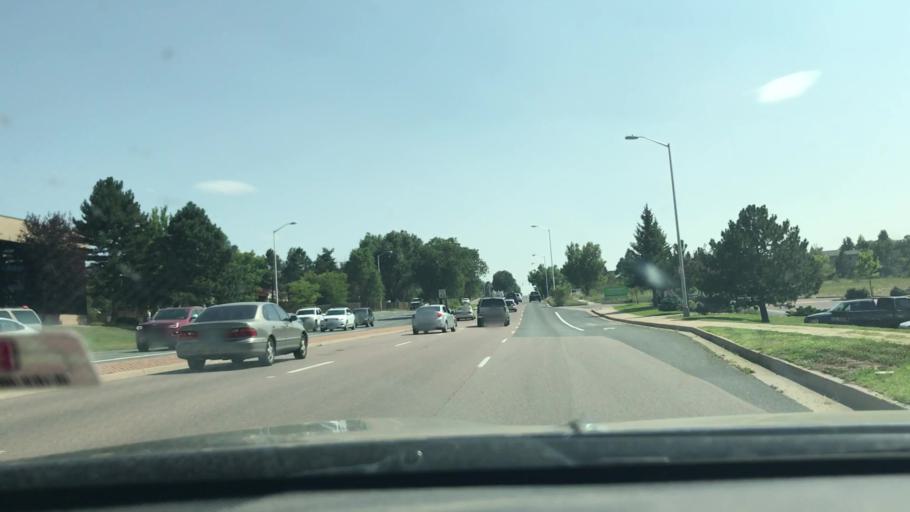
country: US
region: Colorado
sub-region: El Paso County
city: Cimarron Hills
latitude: 38.9255
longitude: -104.7754
